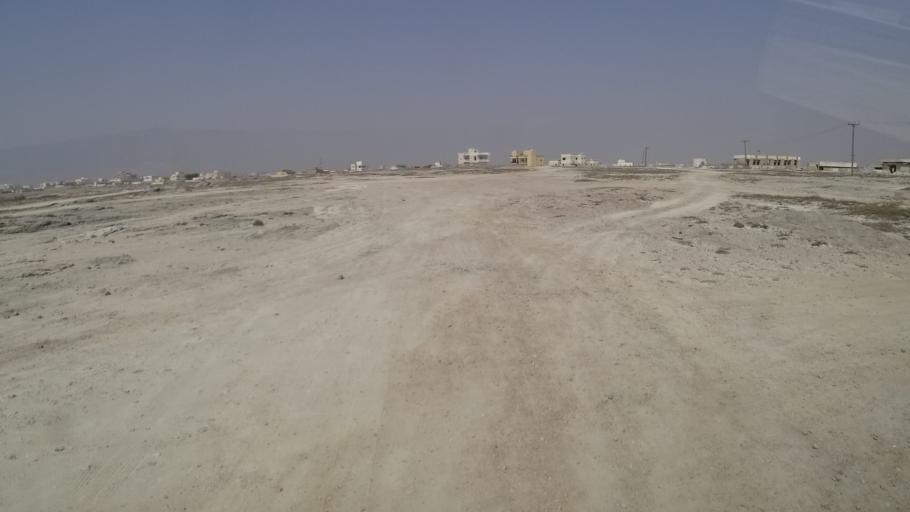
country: OM
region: Zufar
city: Salalah
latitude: 16.9712
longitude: 54.7005
